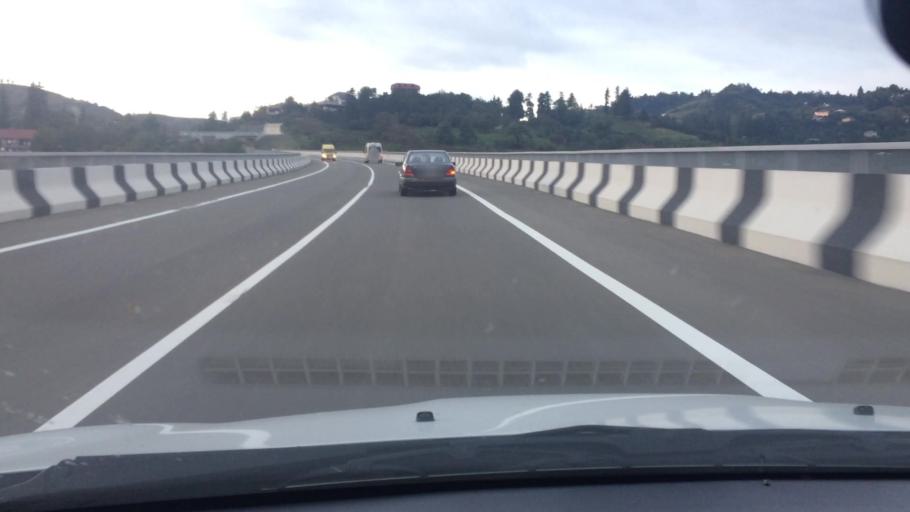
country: GE
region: Ajaria
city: Makhinjauri
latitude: 41.7150
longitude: 41.7519
